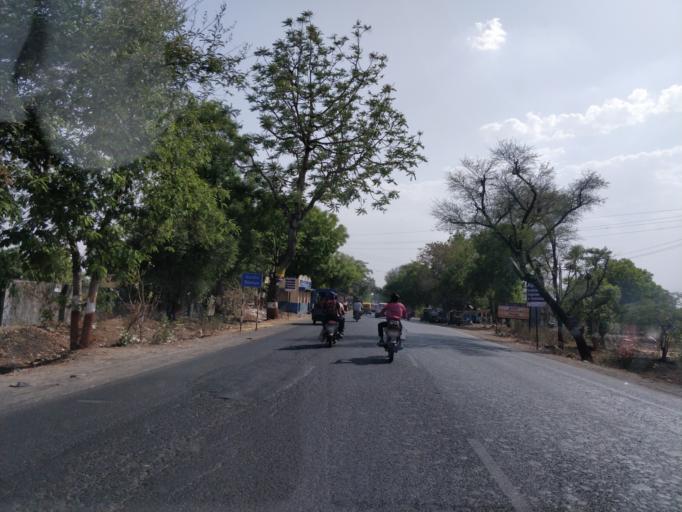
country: IN
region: Gujarat
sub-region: Ahmadabad
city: Naroda
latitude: 23.0913
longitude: 72.6904
